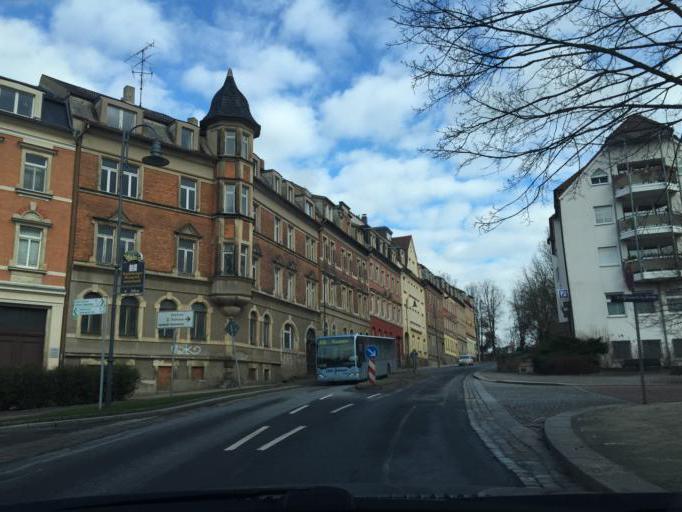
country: DE
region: Saxony
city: Radeberg
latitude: 51.1178
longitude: 13.9169
